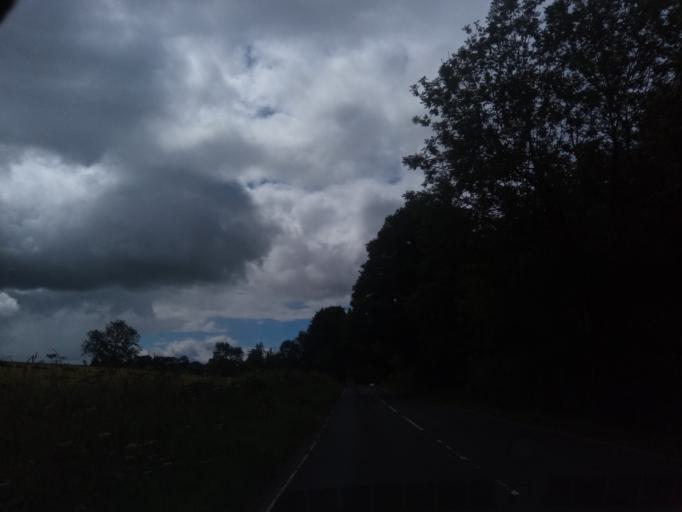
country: GB
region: Scotland
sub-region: Stirling
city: Doune
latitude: 56.1869
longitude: -4.0179
